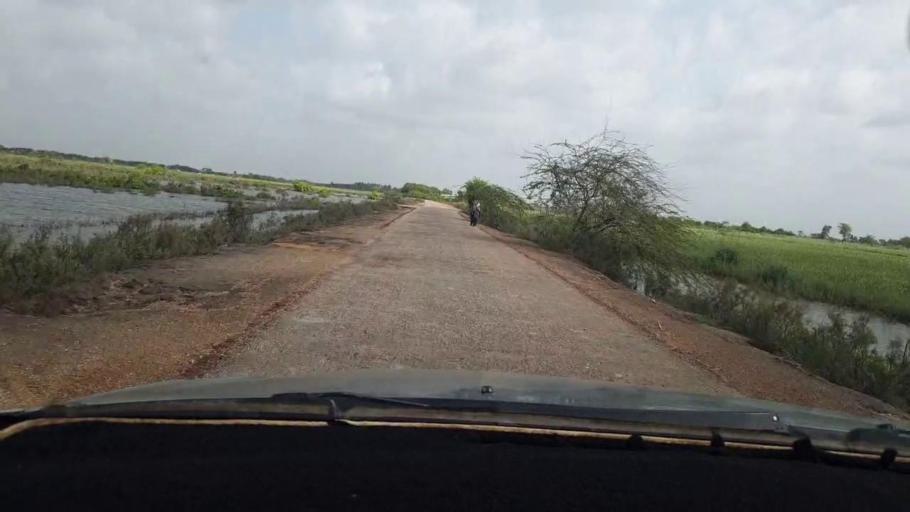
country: PK
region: Sindh
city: Tando Bago
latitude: 24.7856
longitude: 69.0279
